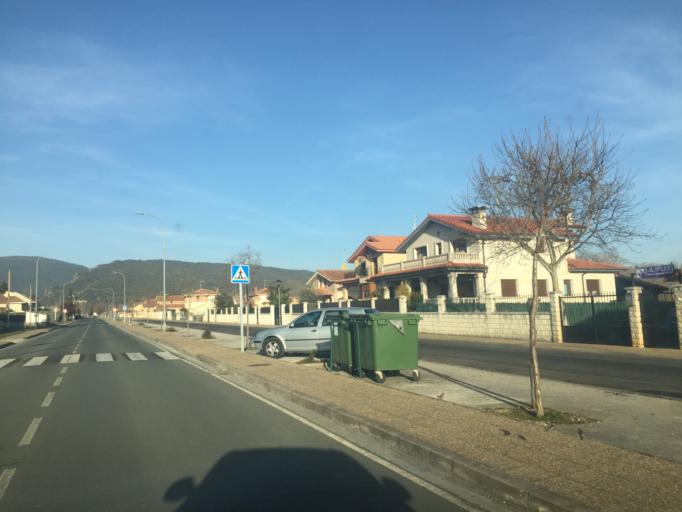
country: ES
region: Castille and Leon
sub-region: Provincia de Burgos
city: Medina de Pomar
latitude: 42.9390
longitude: -3.5849
